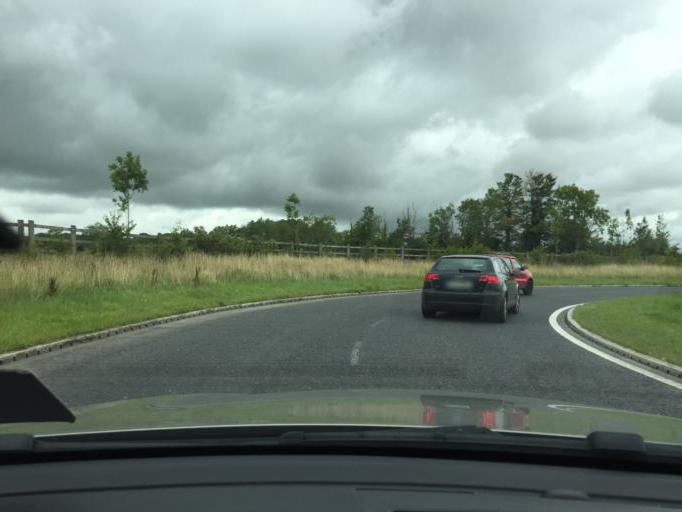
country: IE
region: Leinster
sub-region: An Mhi
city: Dunboyne
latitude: 53.4346
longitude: -6.4742
